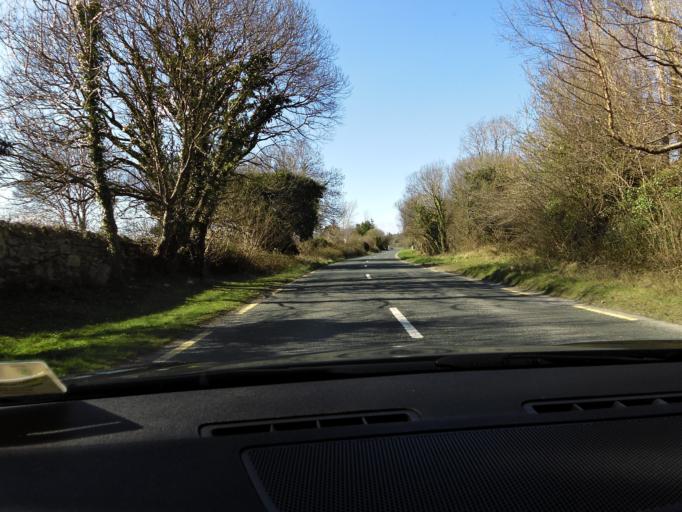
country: IE
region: Connaught
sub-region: County Galway
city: Moycullen
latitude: 53.3533
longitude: -9.2042
